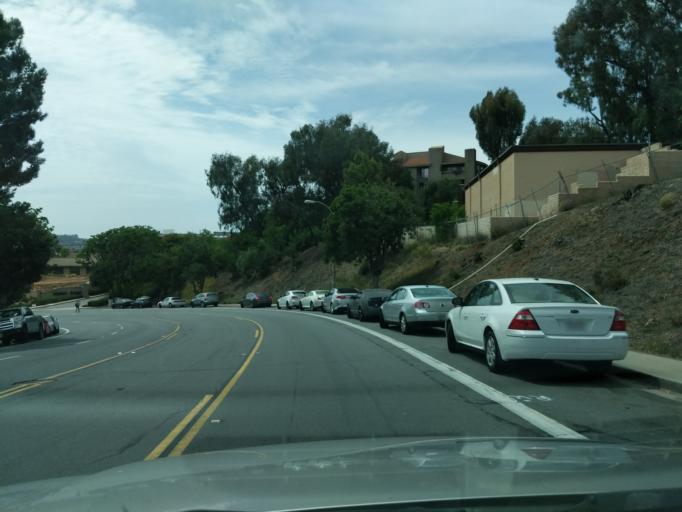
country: US
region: California
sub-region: San Diego County
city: San Diego
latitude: 32.7864
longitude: -117.1095
